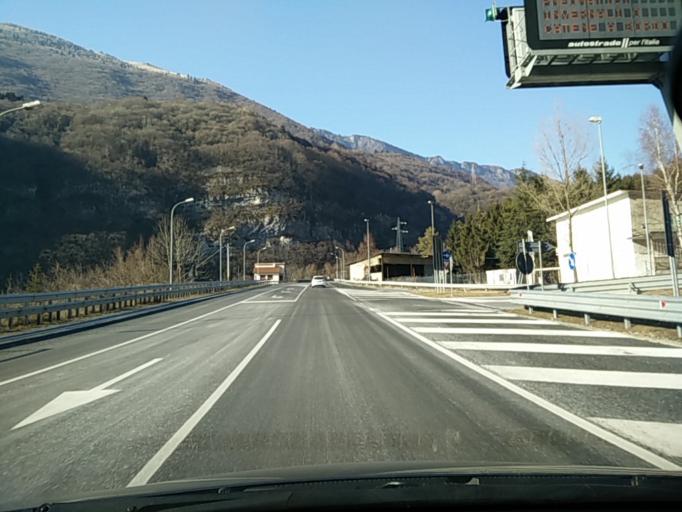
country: IT
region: Veneto
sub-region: Provincia di Belluno
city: Farra d'Alpago
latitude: 46.0755
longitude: 12.3358
